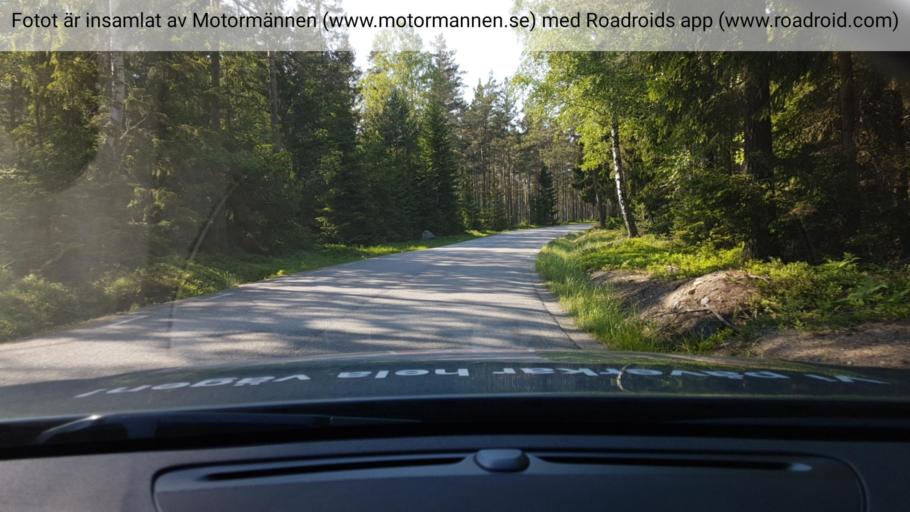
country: SE
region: Stockholm
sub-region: Varmdo Kommun
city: Mortnas
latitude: 59.2520
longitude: 18.4532
